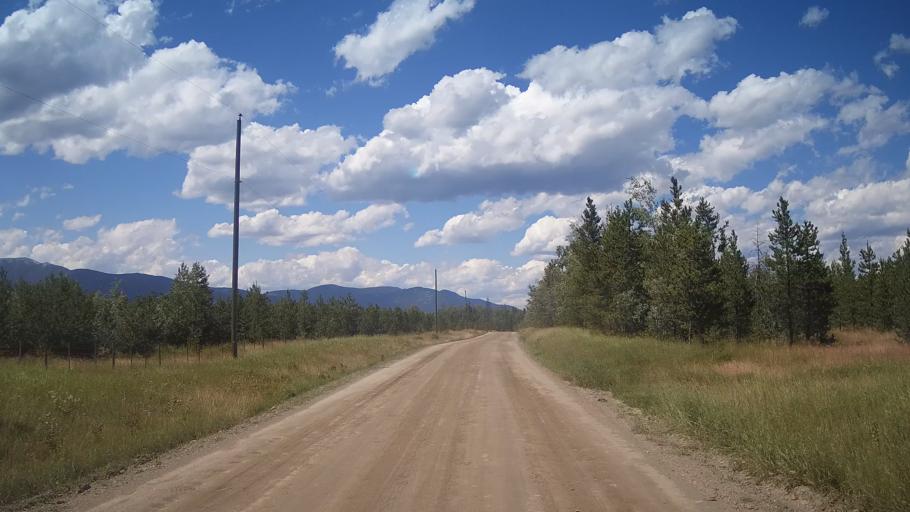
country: CA
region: British Columbia
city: Cache Creek
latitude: 51.2673
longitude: -121.7037
